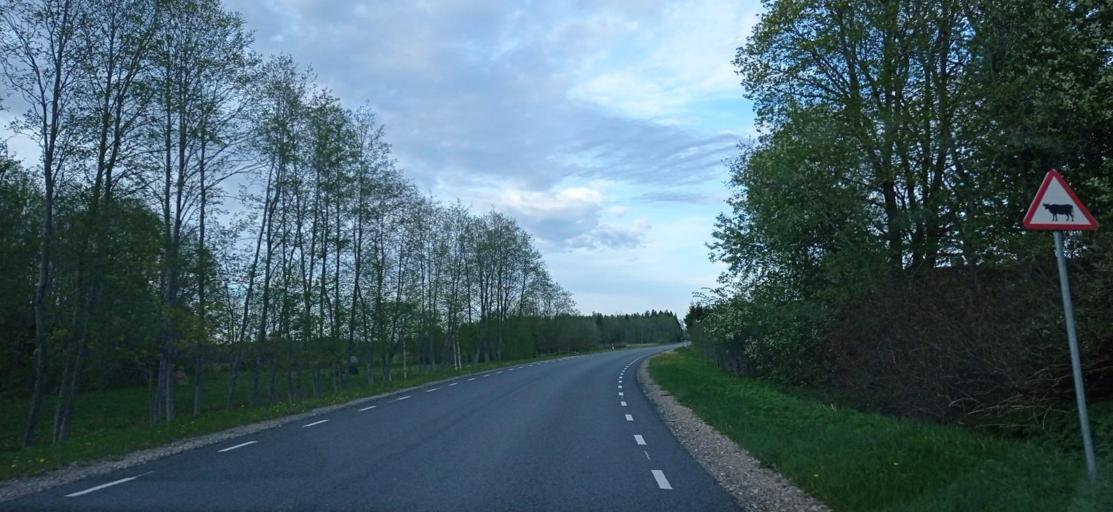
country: EE
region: Paernumaa
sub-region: Tootsi vald
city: Tootsi
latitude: 58.5415
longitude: 24.7394
